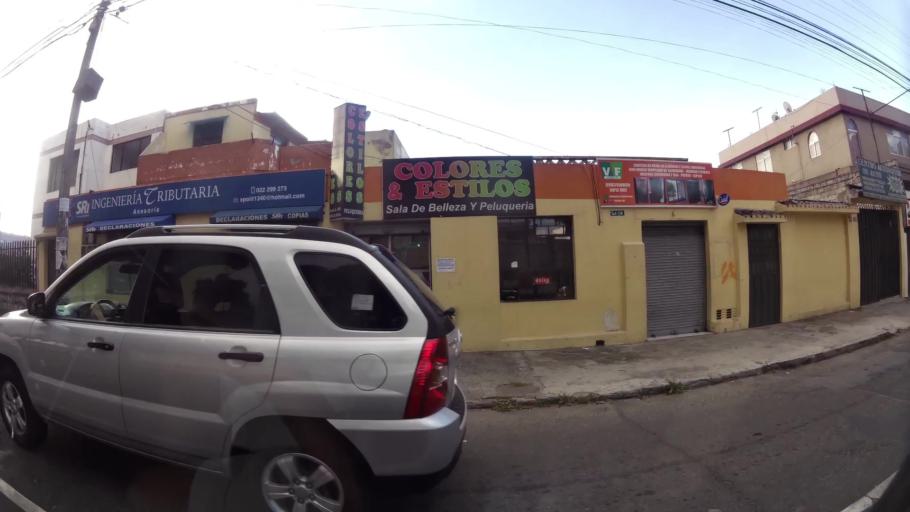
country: EC
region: Pichincha
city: Quito
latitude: -0.1230
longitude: -78.4914
